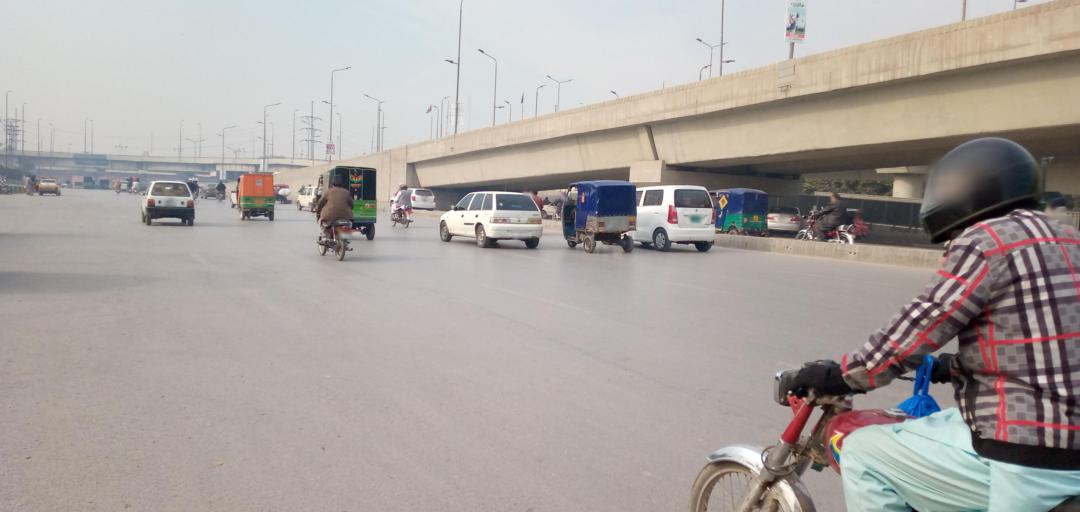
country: PK
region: Khyber Pakhtunkhwa
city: Peshawar
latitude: 34.0143
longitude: 71.5717
